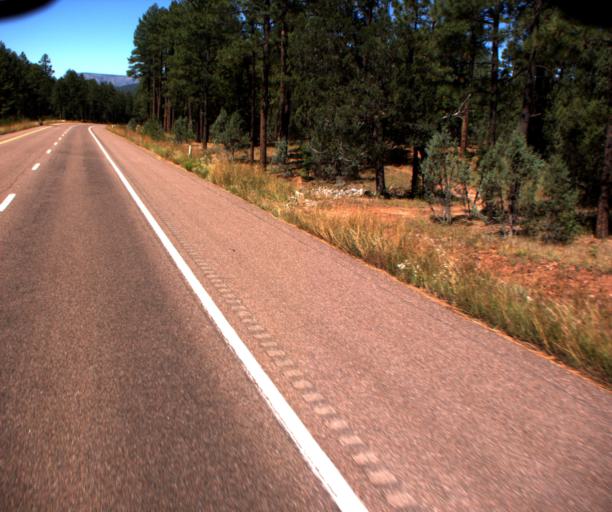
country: US
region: Arizona
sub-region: Gila County
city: Star Valley
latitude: 34.2963
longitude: -110.9824
